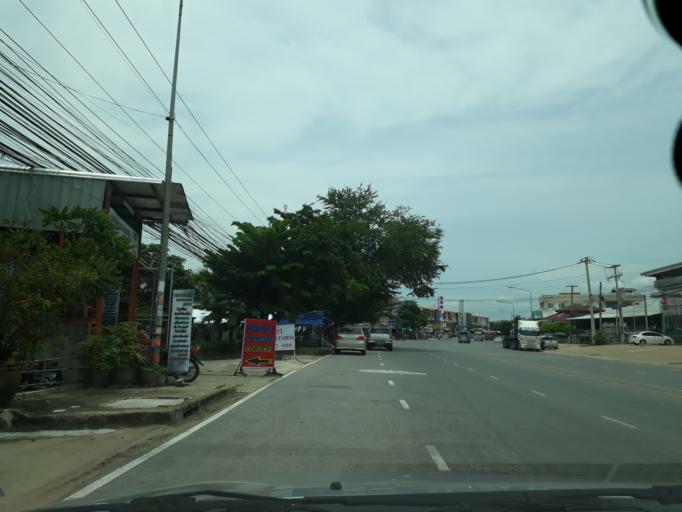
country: TH
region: Khon Kaen
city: Khon Kaen
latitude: 16.4327
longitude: 102.8677
